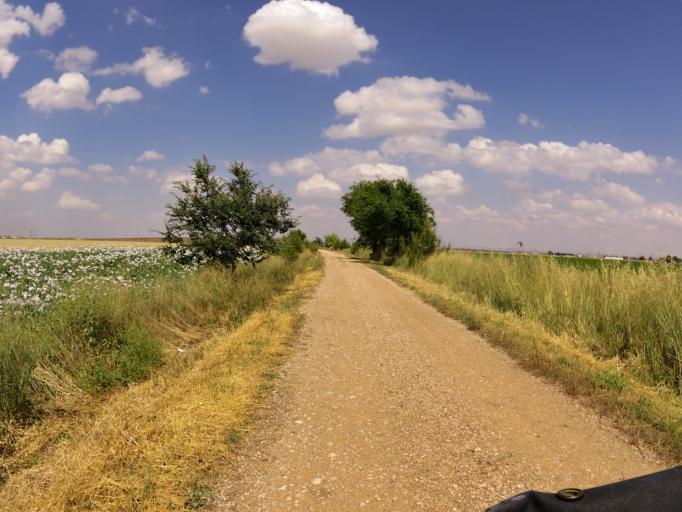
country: ES
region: Castille-La Mancha
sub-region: Provincia de Albacete
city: Pozuelo
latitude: 38.9127
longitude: -2.0172
